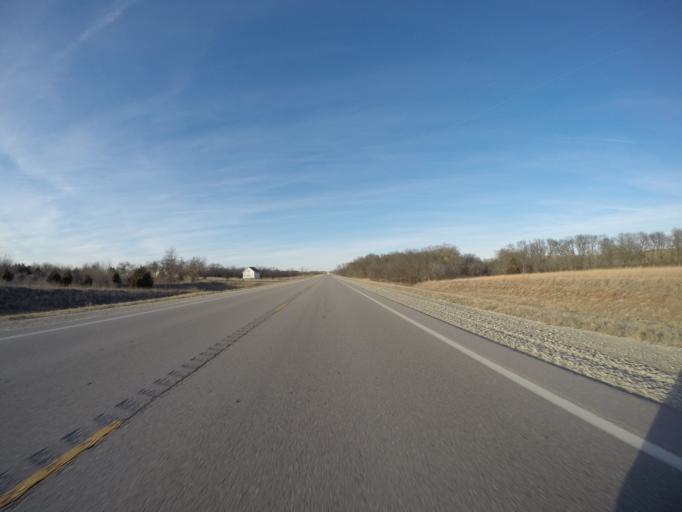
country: US
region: Kansas
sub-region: Marion County
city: Marion
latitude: 38.2603
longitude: -96.9585
